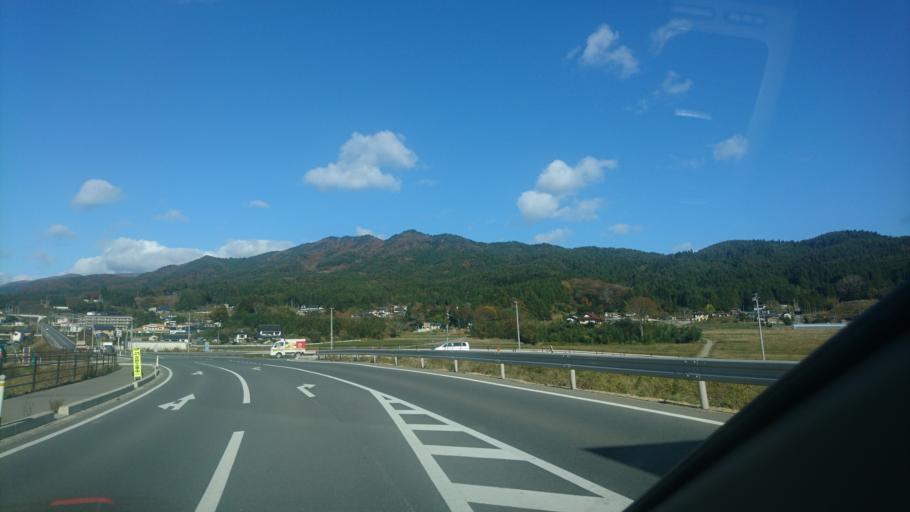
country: JP
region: Iwate
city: Ofunato
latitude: 38.9961
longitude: 141.6926
